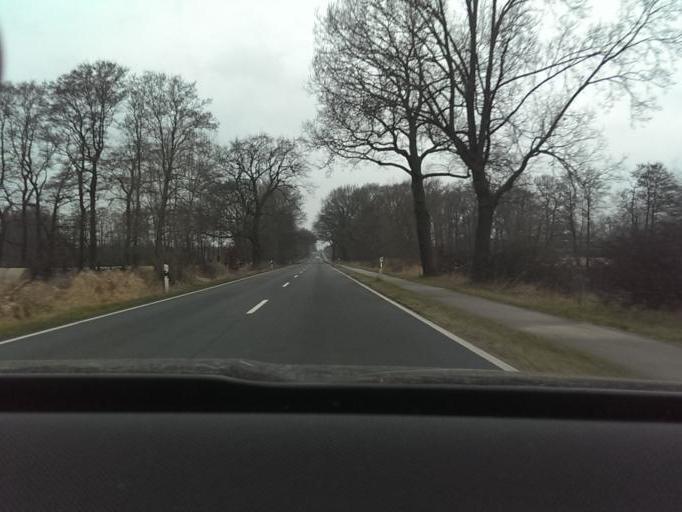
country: DE
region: Lower Saxony
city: Isernhagen Farster Bauerschaft
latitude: 52.5007
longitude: 9.8330
